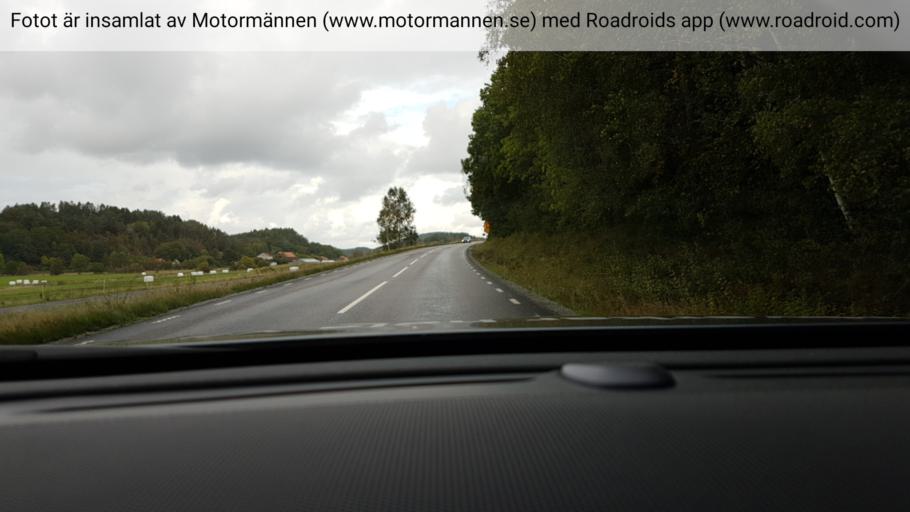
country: SE
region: Vaestra Goetaland
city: Svanesund
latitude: 58.1116
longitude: 11.8506
